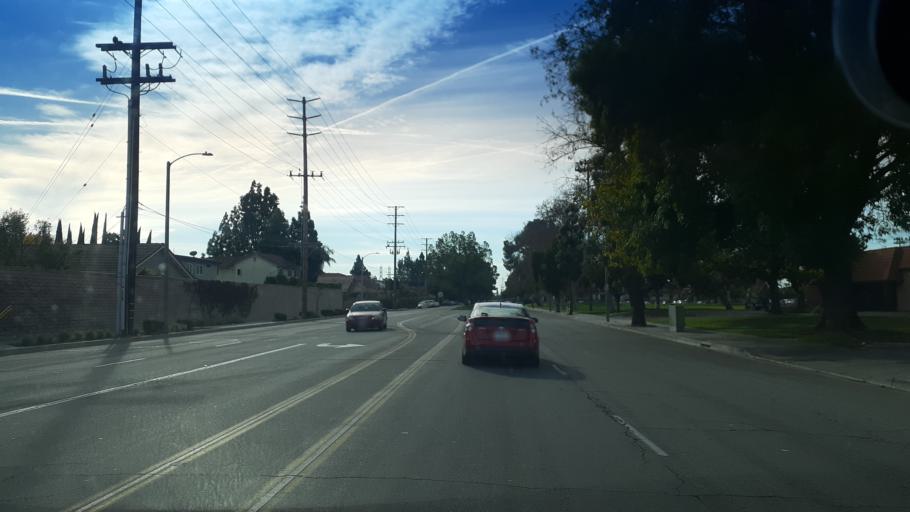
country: US
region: California
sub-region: Los Angeles County
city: Artesia
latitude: 33.8577
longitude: -118.0996
